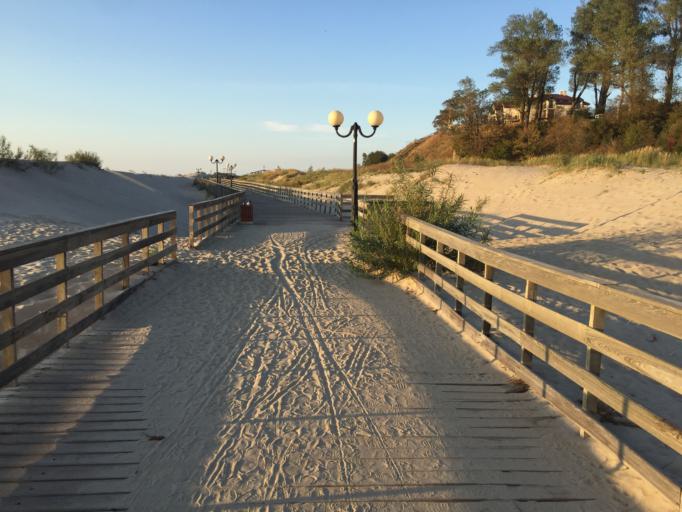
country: RU
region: Kaliningrad
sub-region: Gorod Kaliningrad
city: Yantarnyy
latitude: 54.8723
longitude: 19.9337
